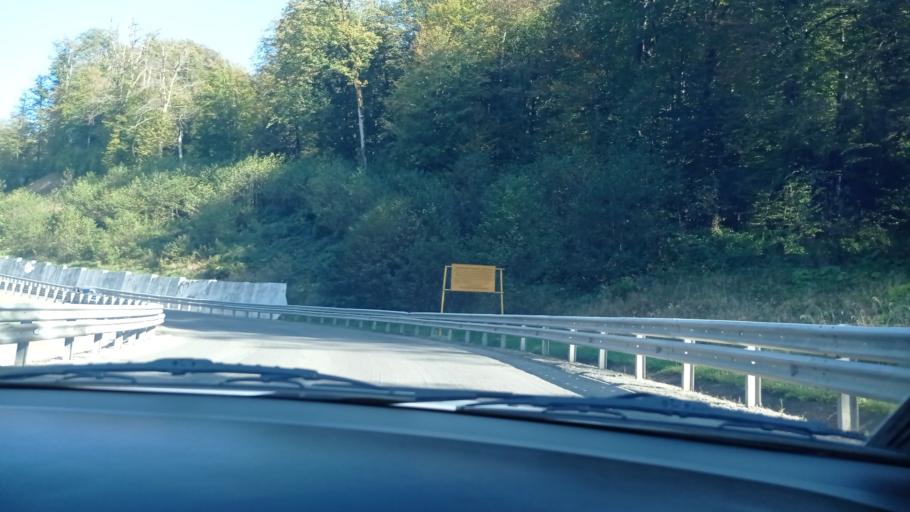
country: RU
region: Krasnodarskiy
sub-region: Sochi City
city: Krasnaya Polyana
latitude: 43.6587
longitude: 40.3028
